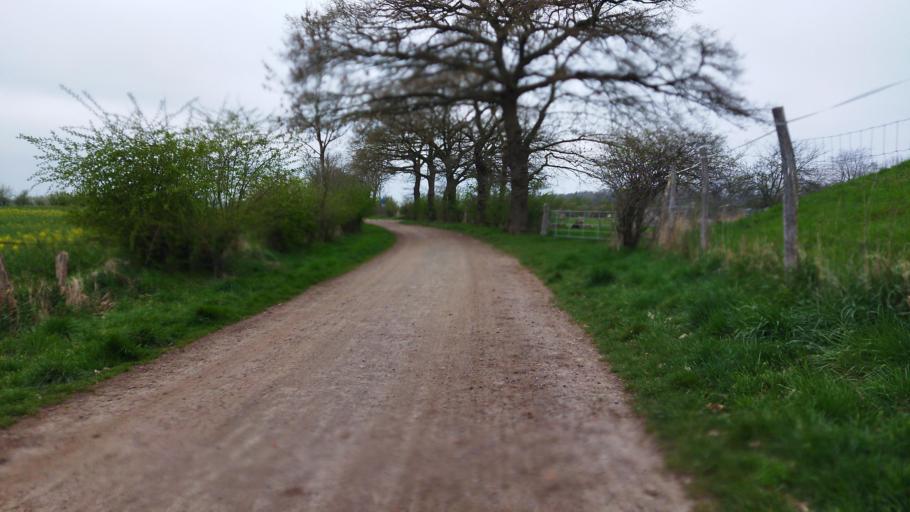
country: DE
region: Lower Saxony
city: Achim
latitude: 53.0090
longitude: 9.0068
